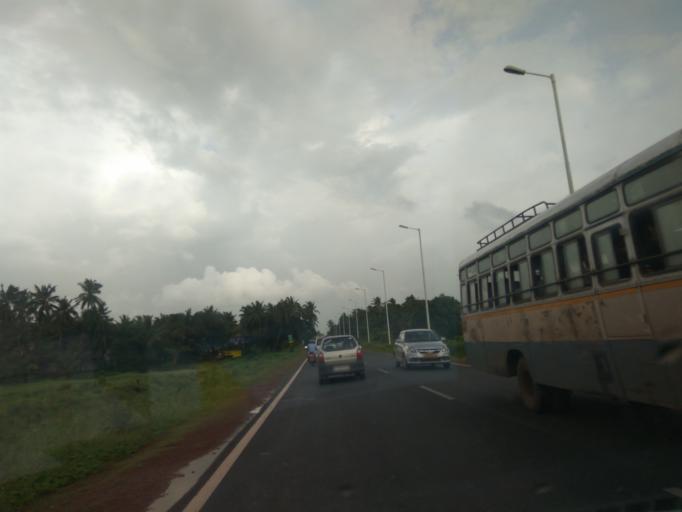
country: IN
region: Goa
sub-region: North Goa
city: Goa Velha
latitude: 15.4276
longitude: 73.8926
